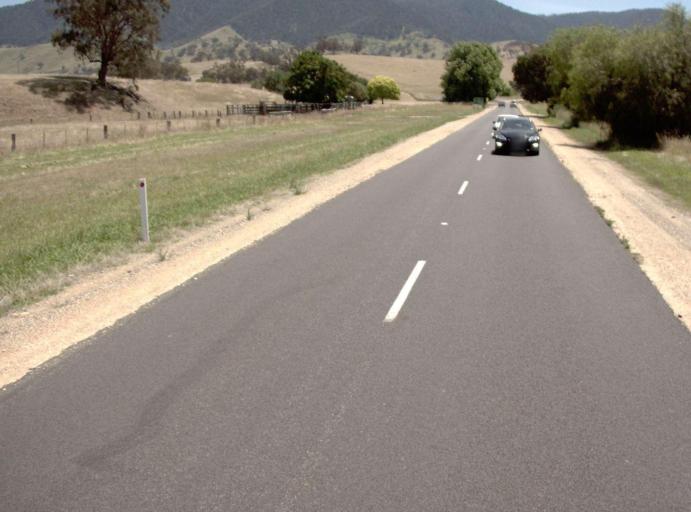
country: AU
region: Victoria
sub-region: East Gippsland
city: Bairnsdale
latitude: -37.1963
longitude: 147.7234
